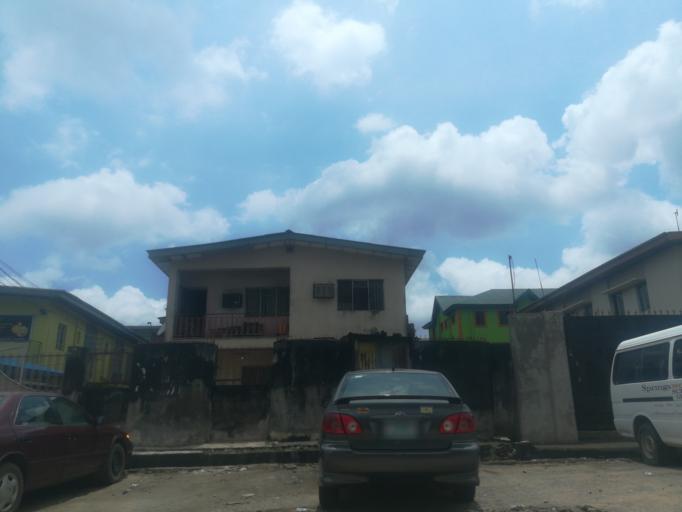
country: NG
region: Lagos
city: Somolu
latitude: 6.5580
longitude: 3.3917
